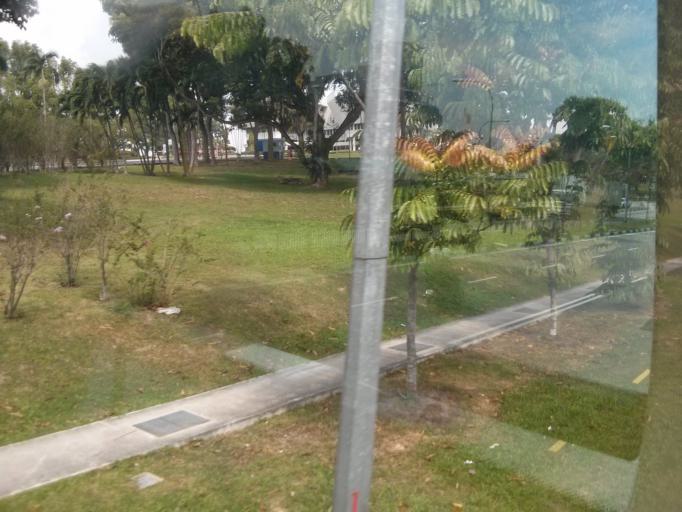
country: SG
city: Singapore
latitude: 1.3285
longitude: 103.7441
